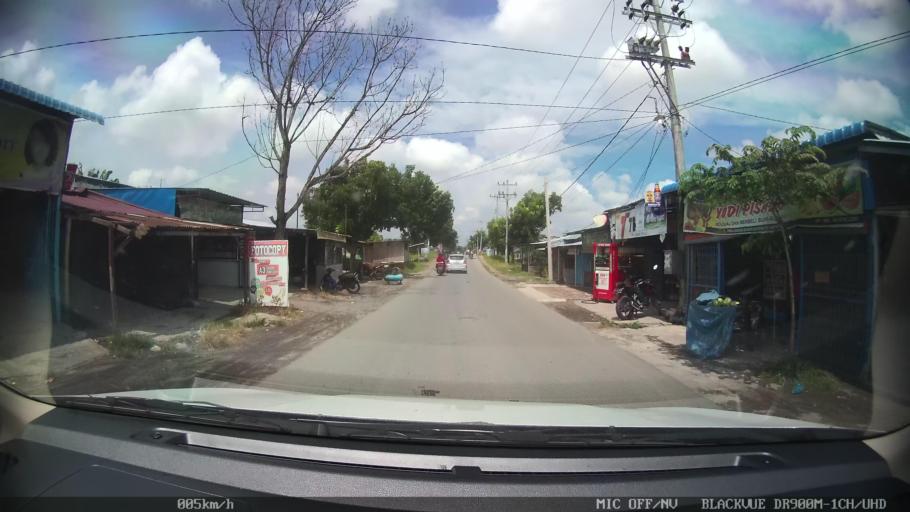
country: ID
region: North Sumatra
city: Percut
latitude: 3.6199
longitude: 98.7811
